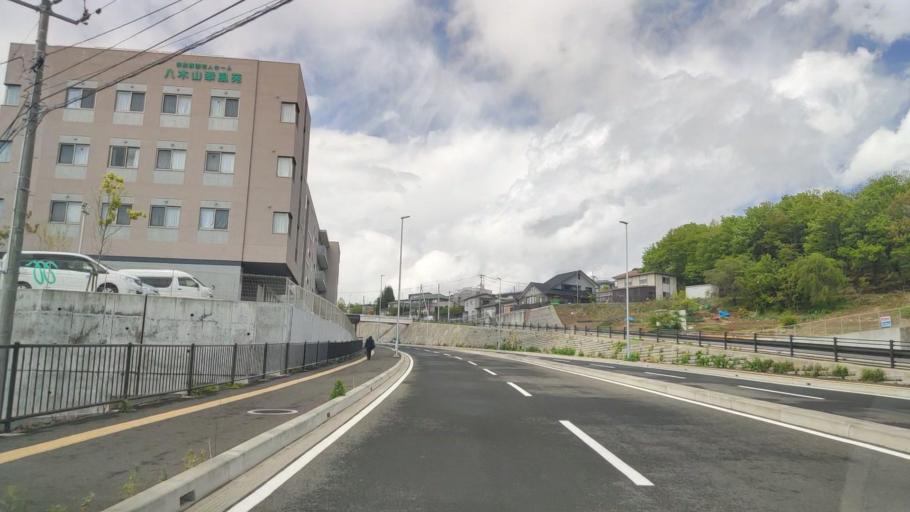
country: JP
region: Miyagi
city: Sendai
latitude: 38.2345
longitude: 140.8525
